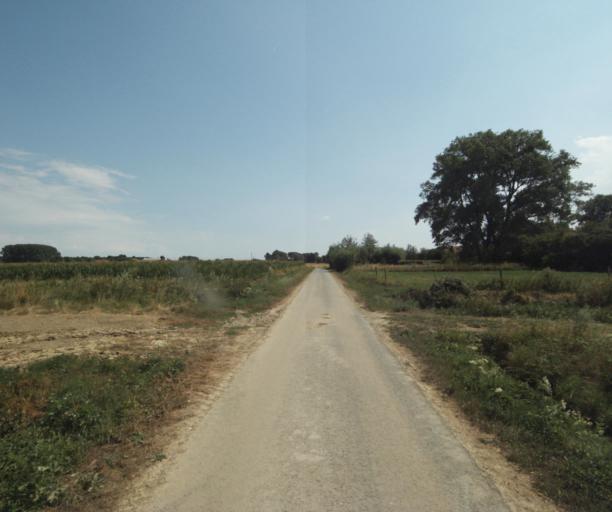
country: FR
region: Nord-Pas-de-Calais
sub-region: Departement du Nord
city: Quesnoy-sur-Deule
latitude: 50.7314
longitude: 2.9911
